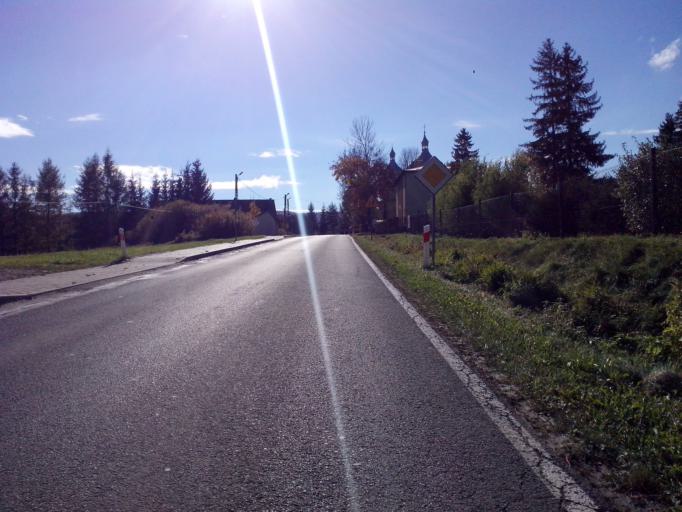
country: PL
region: Subcarpathian Voivodeship
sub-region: Powiat strzyzowski
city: Jawornik
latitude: 49.7818
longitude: 21.8552
